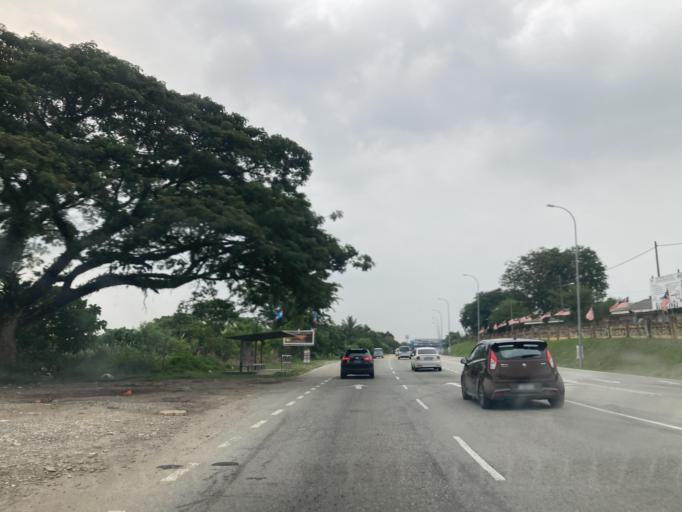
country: MY
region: Selangor
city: Kuang
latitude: 3.2047
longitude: 101.5439
